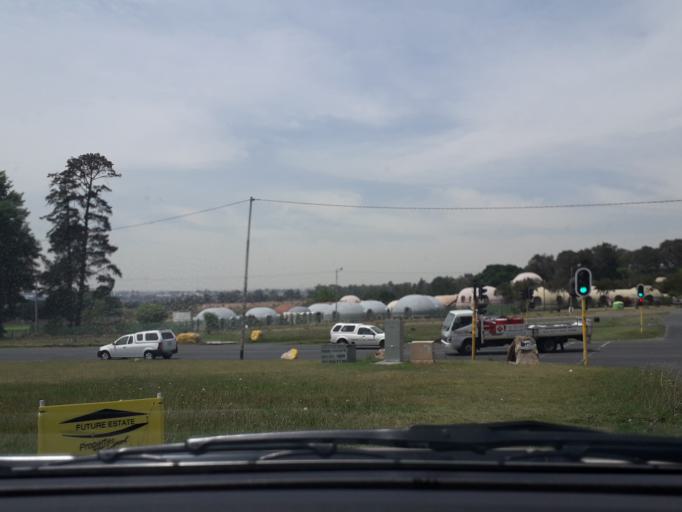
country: ZA
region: Gauteng
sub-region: City of Johannesburg Metropolitan Municipality
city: Roodepoort
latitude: -26.1819
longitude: 27.9275
